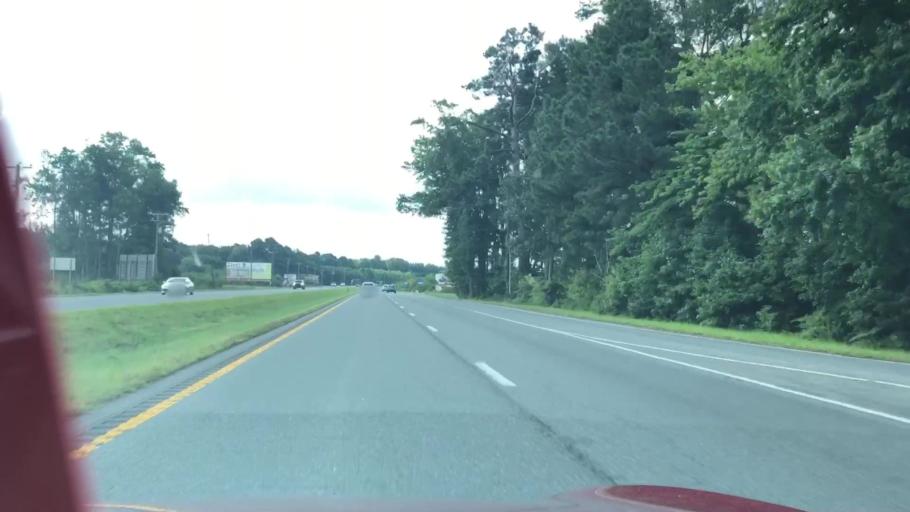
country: US
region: Virginia
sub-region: Accomack County
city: Wattsville
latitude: 37.9880
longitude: -75.5331
